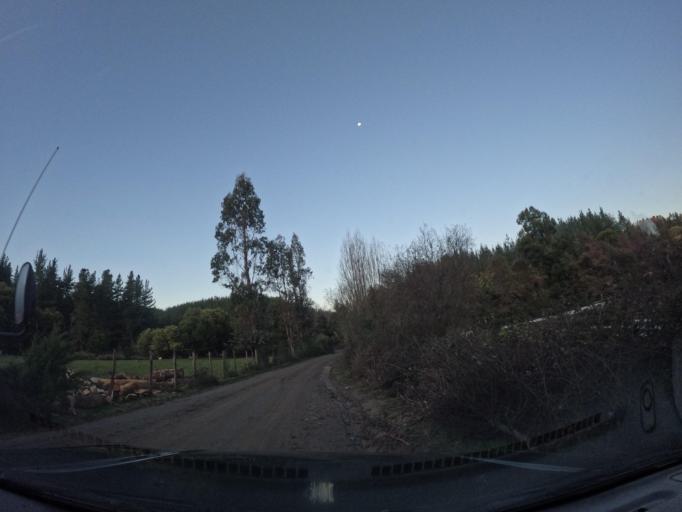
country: CL
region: Biobio
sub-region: Provincia de Concepcion
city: Chiguayante
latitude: -36.9935
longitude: -72.8358
